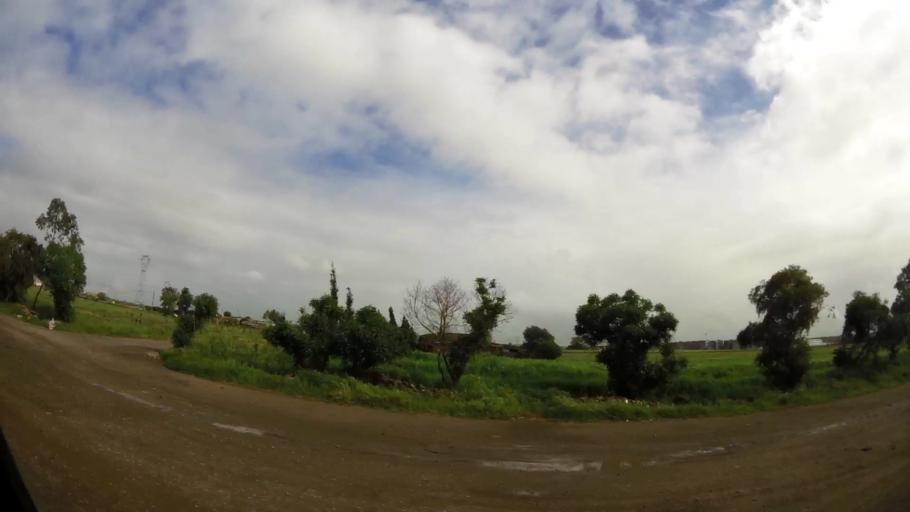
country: MA
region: Grand Casablanca
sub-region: Mohammedia
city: Mohammedia
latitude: 33.6500
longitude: -7.4144
